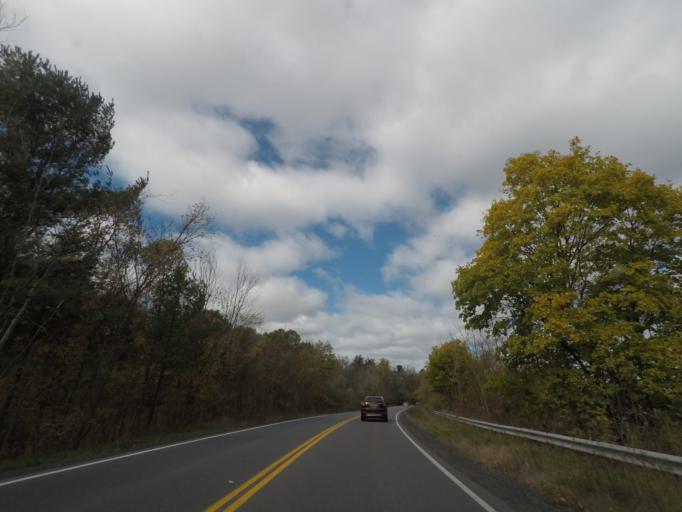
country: US
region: New York
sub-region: Albany County
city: Cohoes
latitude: 42.7990
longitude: -73.7193
